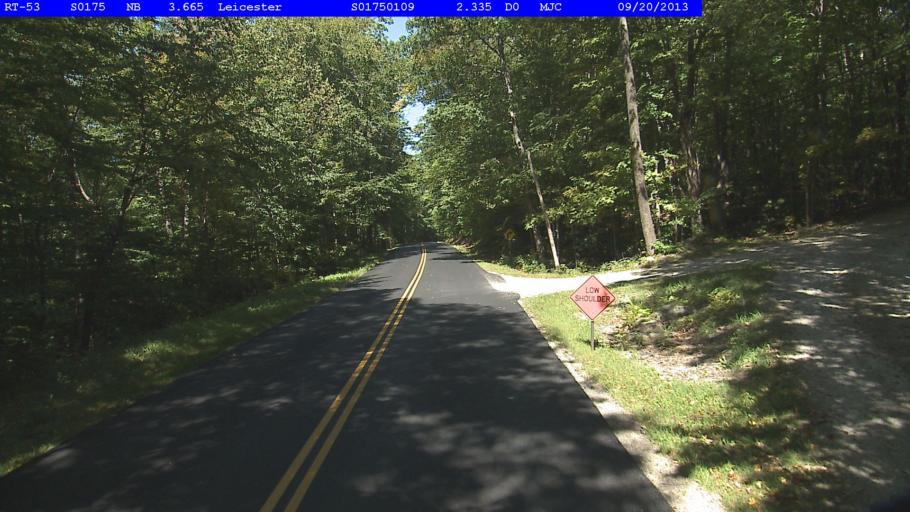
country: US
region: Vermont
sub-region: Rutland County
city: Brandon
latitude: 43.8764
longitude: -73.0637
